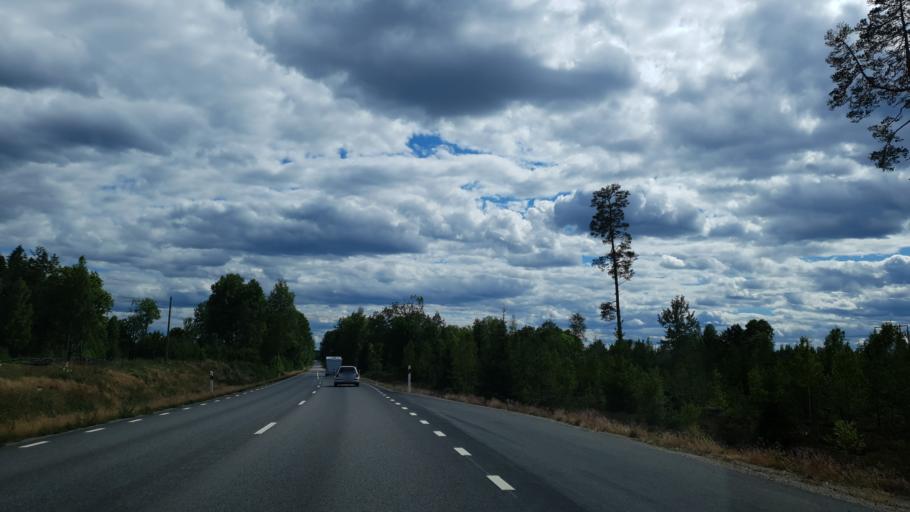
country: SE
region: Kronoberg
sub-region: Lessebo Kommun
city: Lessebo
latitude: 56.7978
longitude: 15.4120
